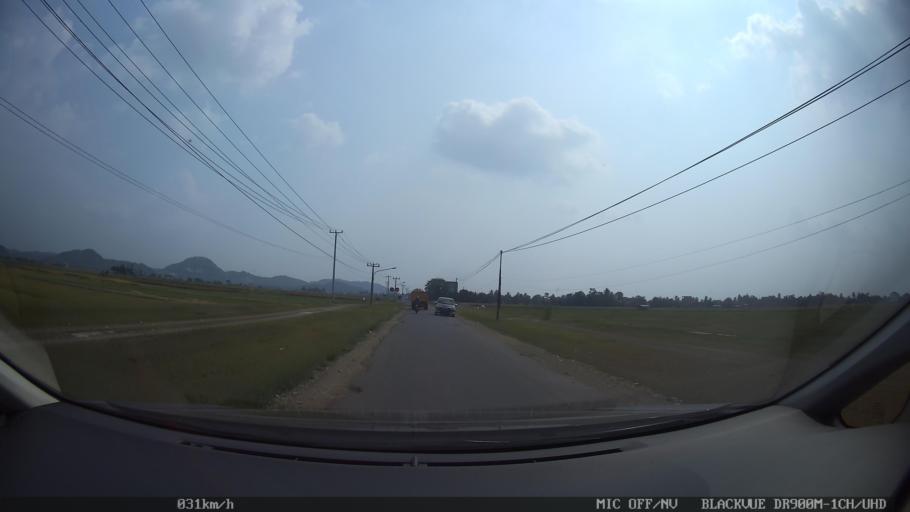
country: ID
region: Lampung
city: Pringsewu
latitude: -5.3567
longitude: 105.0107
